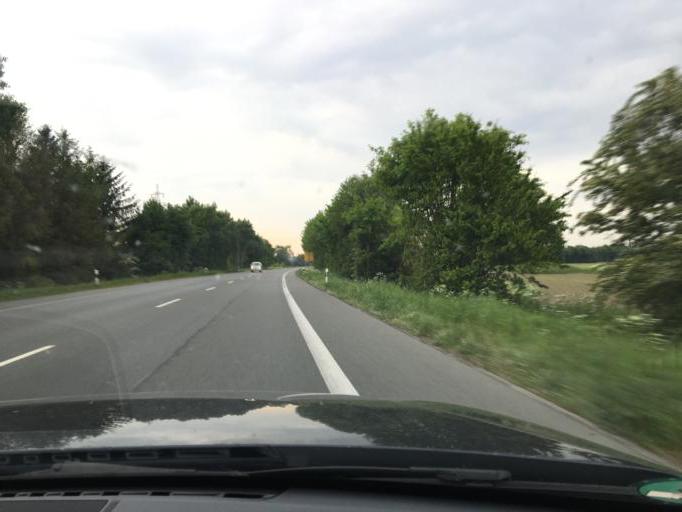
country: DE
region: North Rhine-Westphalia
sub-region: Regierungsbezirk Munster
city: Greven
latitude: 52.1298
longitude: 7.5783
